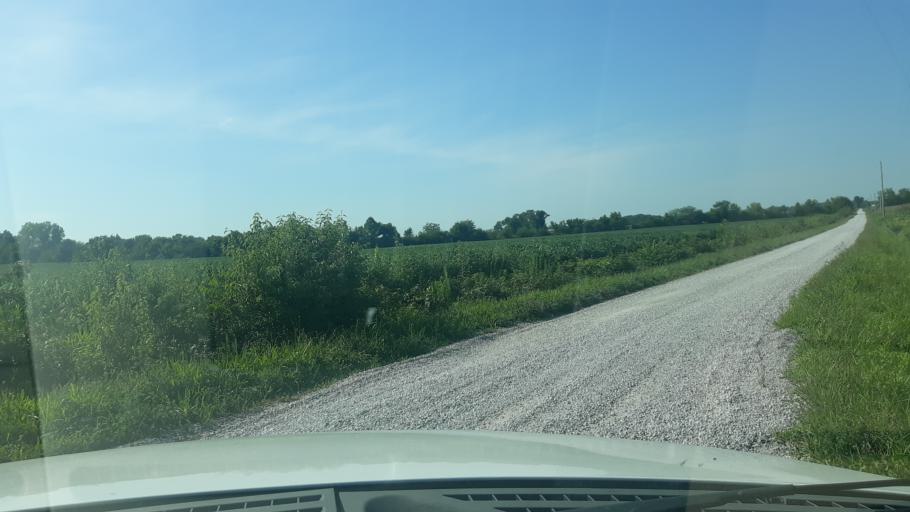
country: US
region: Illinois
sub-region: Saline County
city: Eldorado
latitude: 37.8468
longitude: -88.4849
